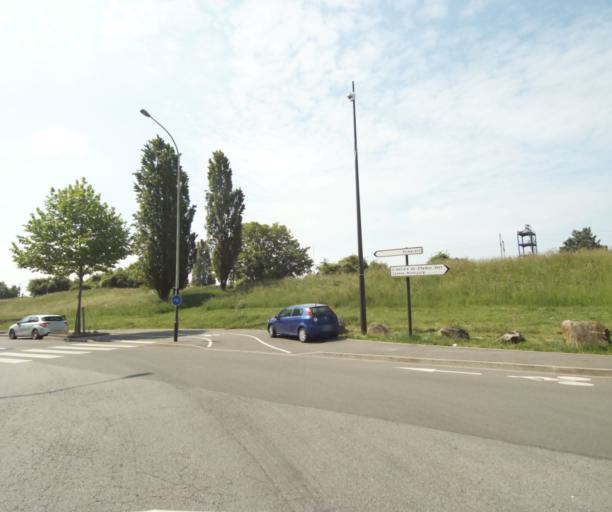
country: FR
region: Ile-de-France
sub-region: Departement du Val-d'Oise
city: Cormeilles-en-Parisis
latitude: 48.9544
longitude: 2.2163
